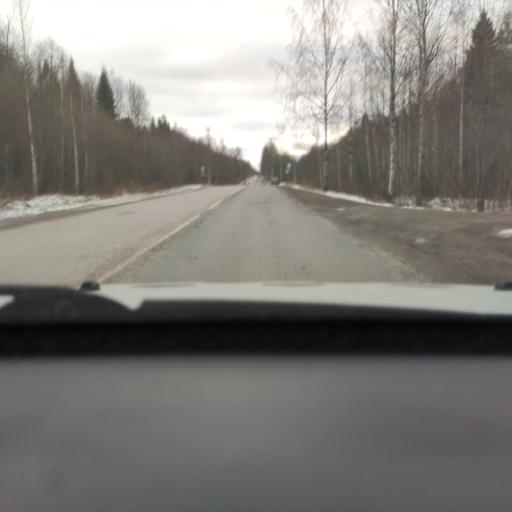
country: RU
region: Perm
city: Polazna
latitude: 58.1073
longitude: 56.4196
